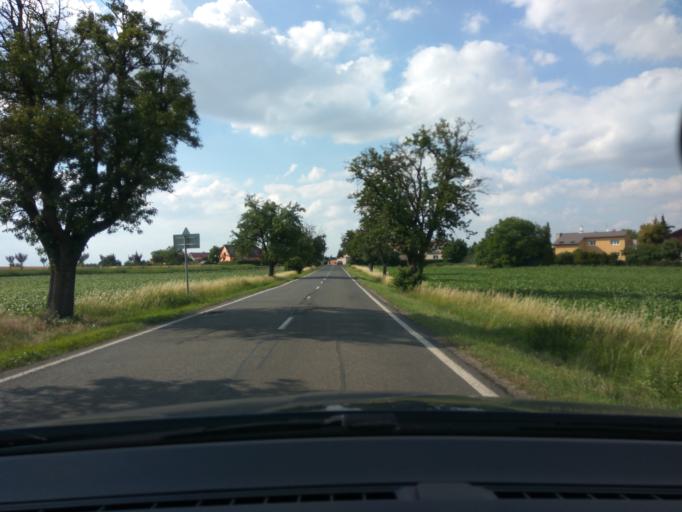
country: CZ
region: Praha
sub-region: Praha 19
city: Kbely
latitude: 50.1522
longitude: 14.5417
